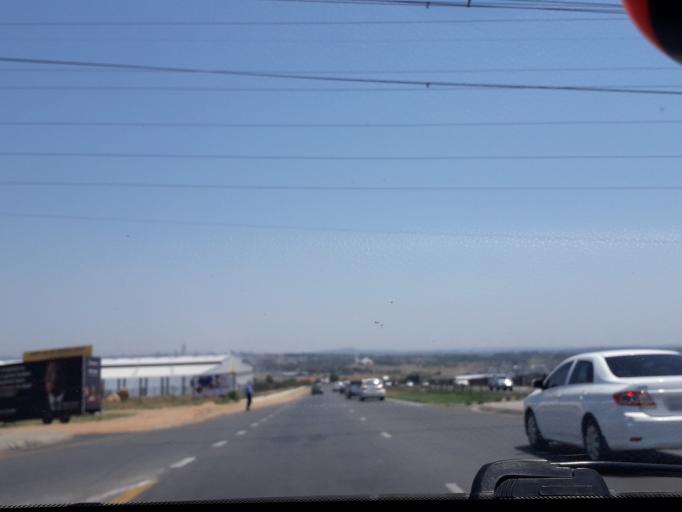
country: ZA
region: Gauteng
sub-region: City of Johannesburg Metropolitan Municipality
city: Midrand
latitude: -26.0193
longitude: 28.1225
